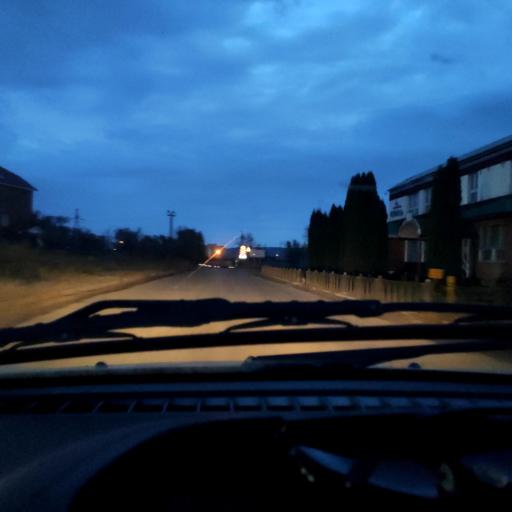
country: RU
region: Samara
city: Zhigulevsk
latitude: 53.4753
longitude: 49.4994
